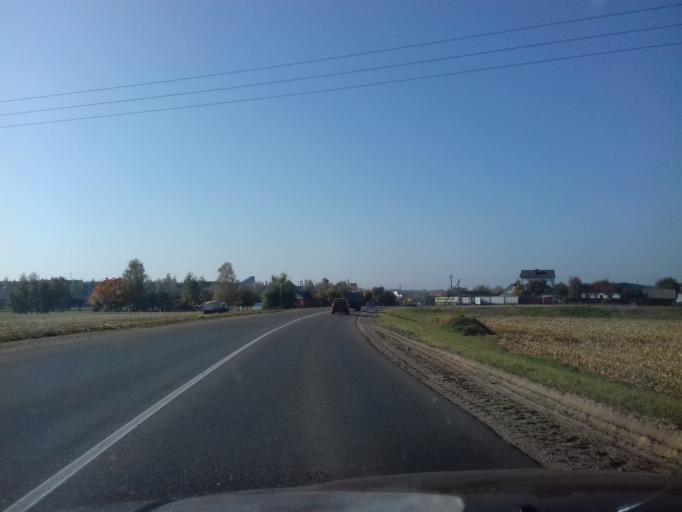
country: BY
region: Minsk
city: Hatava
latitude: 53.7798
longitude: 27.6526
